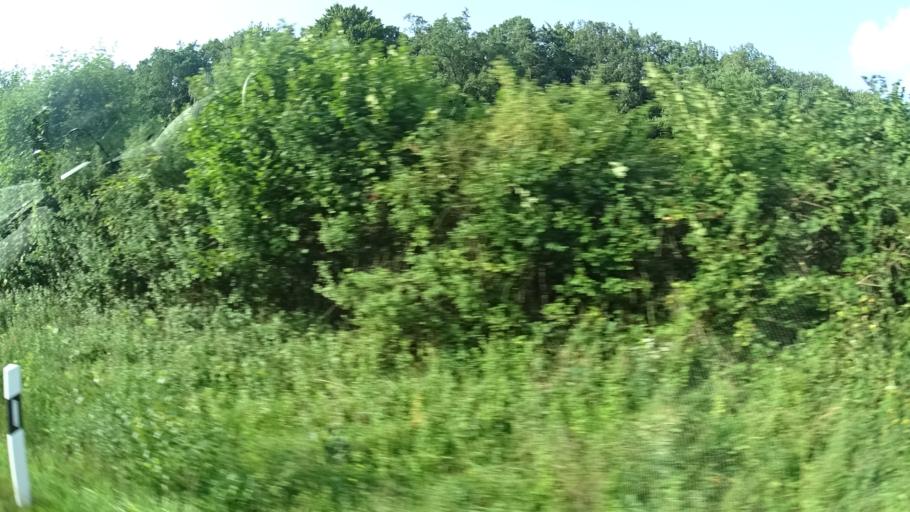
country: DE
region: Hesse
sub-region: Regierungsbezirk Darmstadt
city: Beerfelden
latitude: 49.5507
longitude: 9.0070
